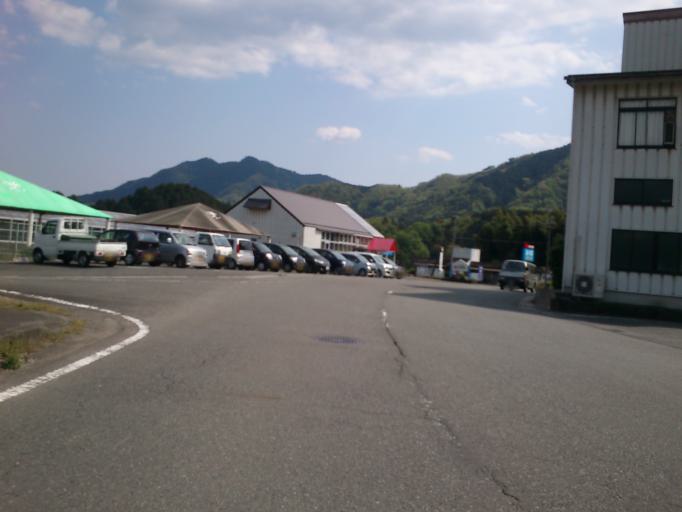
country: JP
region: Kyoto
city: Fukuchiyama
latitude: 35.3353
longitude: 134.9302
